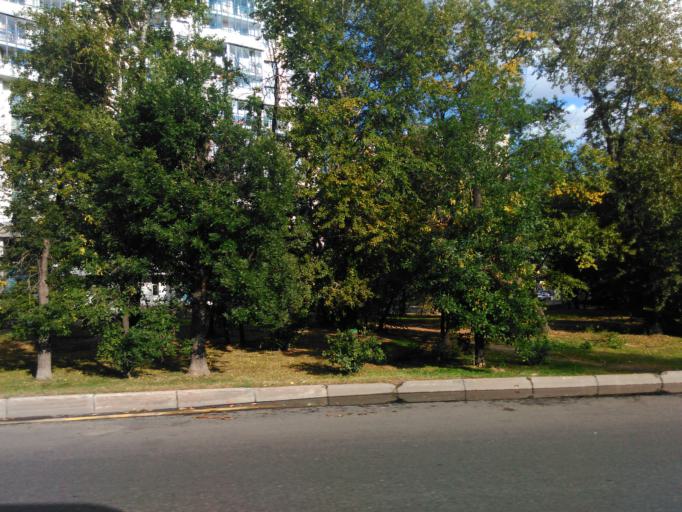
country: RU
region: Moscow
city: Zapadnoye Degunino
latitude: 55.8694
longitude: 37.5476
